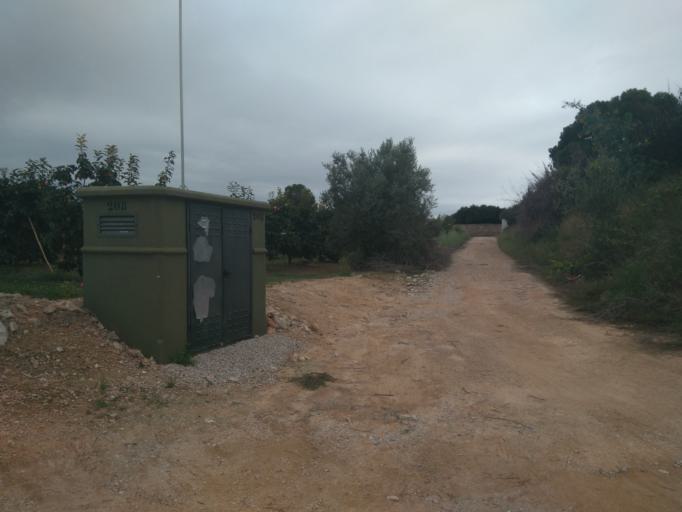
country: ES
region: Valencia
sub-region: Provincia de Valencia
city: Benimodo
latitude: 39.1975
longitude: -0.5704
